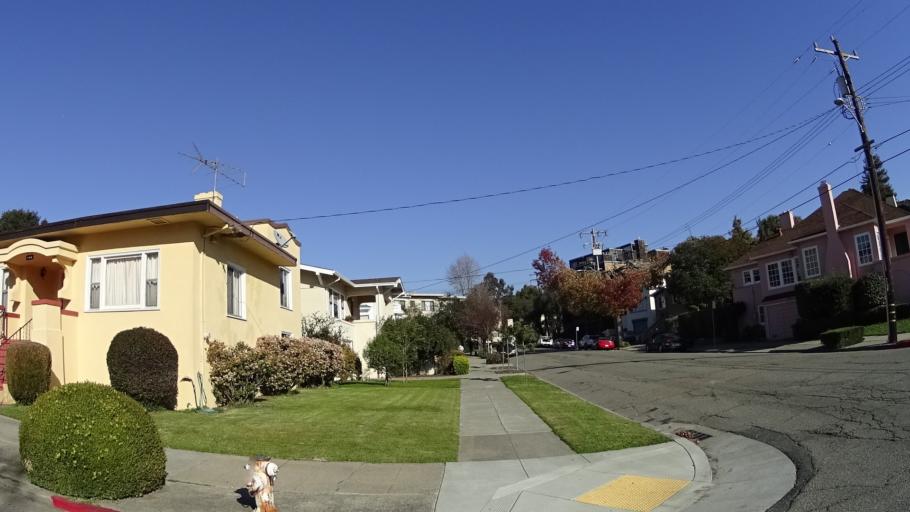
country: US
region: California
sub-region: Alameda County
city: Piedmont
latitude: 37.8064
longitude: -122.2424
